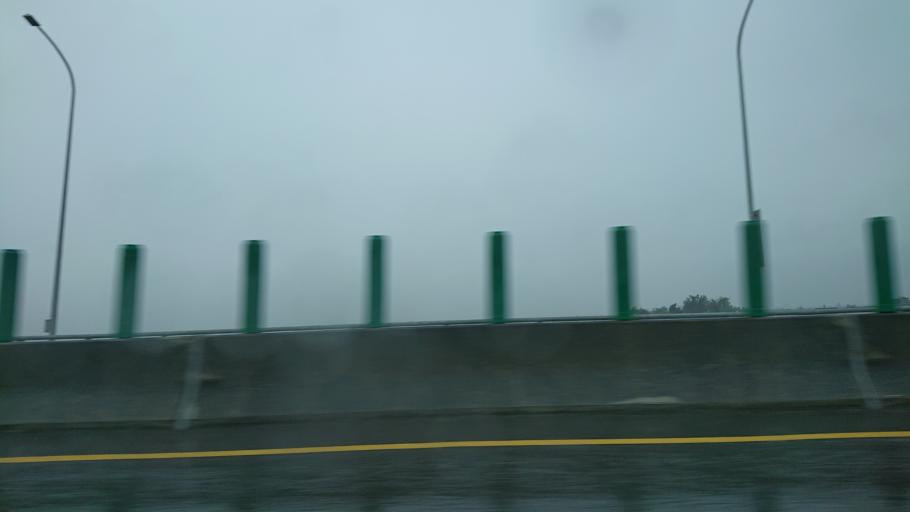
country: TW
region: Taiwan
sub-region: Yunlin
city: Douliu
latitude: 23.7812
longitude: 120.2743
